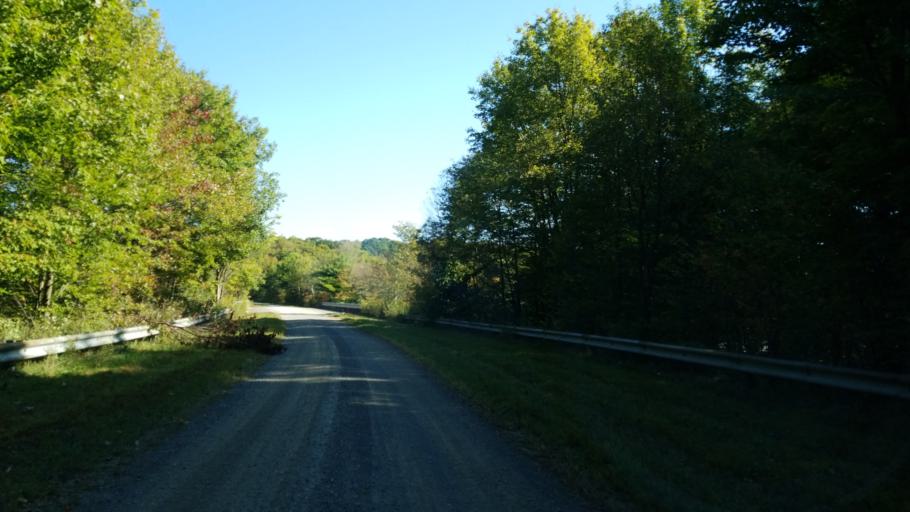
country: US
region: Pennsylvania
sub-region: Clearfield County
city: Curwensville
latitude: 41.1233
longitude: -78.5665
